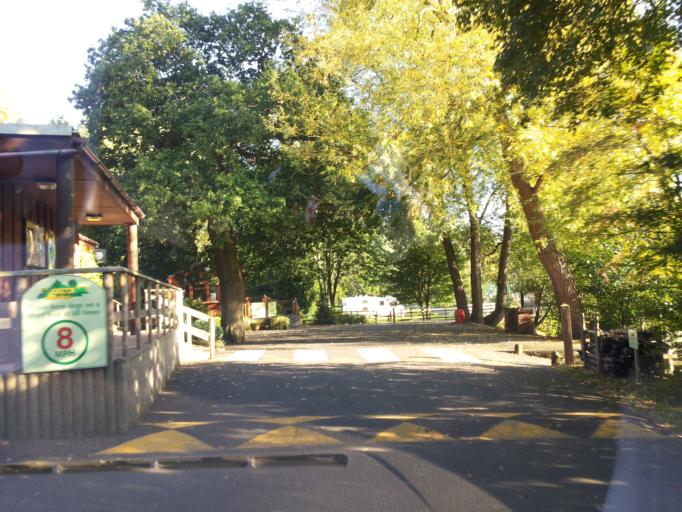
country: GB
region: England
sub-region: Worcestershire
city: Stourport-on-Severn
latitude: 52.3452
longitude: -2.2967
